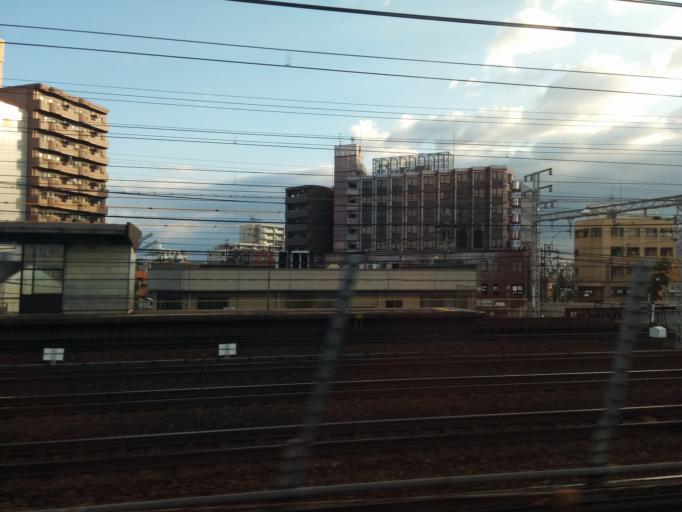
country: JP
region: Aichi
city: Nagoya-shi
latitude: 35.1833
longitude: 136.8730
